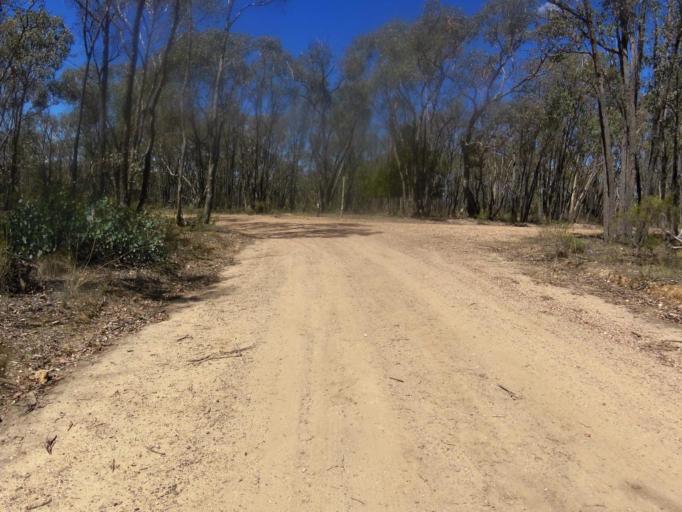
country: AU
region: Victoria
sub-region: Mount Alexander
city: Castlemaine
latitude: -37.0125
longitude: 144.1273
